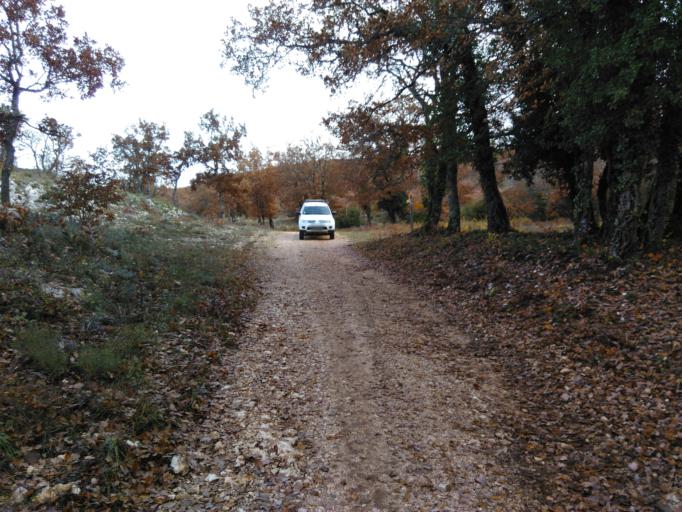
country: FR
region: Provence-Alpes-Cote d'Azur
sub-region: Departement du Vaucluse
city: Gordes
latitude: 43.9829
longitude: 5.2239
